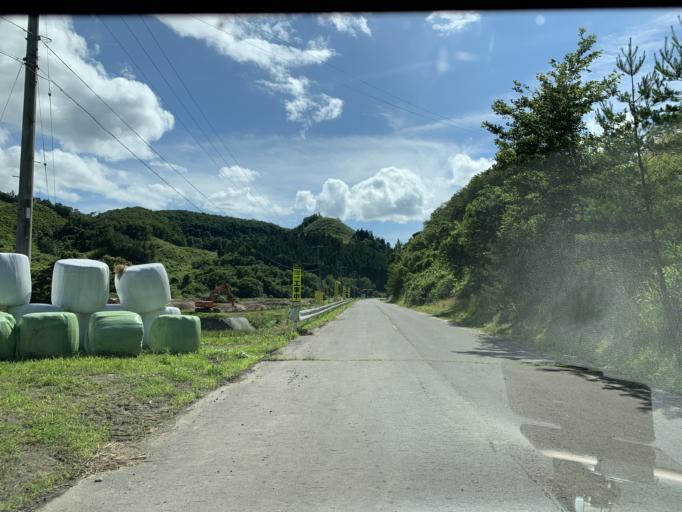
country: JP
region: Iwate
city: Ichinoseki
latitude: 38.9626
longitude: 140.9624
